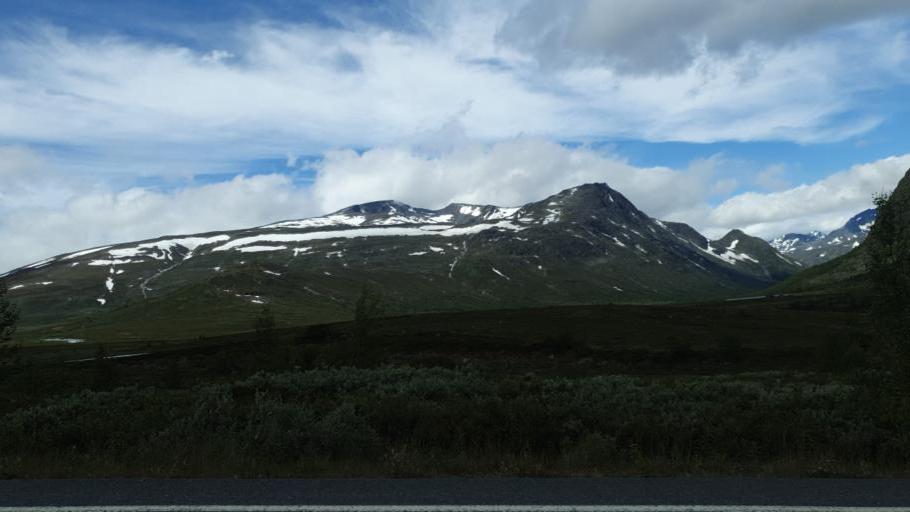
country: NO
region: Oppland
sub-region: Vang
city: Vang
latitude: 61.4612
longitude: 8.8064
